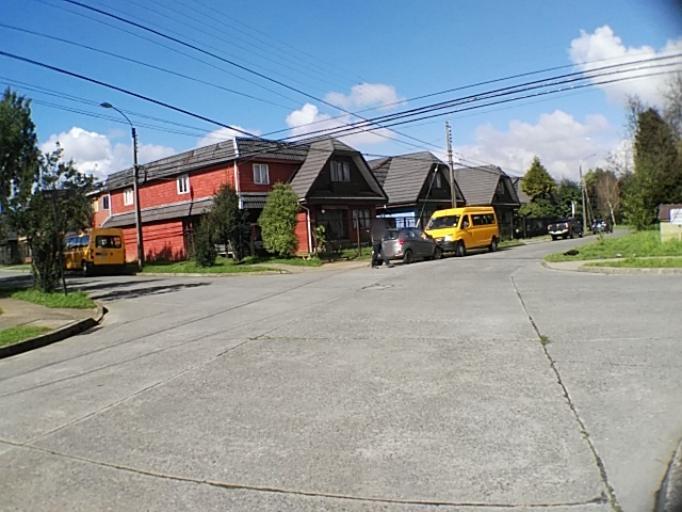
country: CL
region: Los Rios
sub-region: Provincia de Valdivia
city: Valdivia
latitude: -39.8327
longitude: -73.2310
